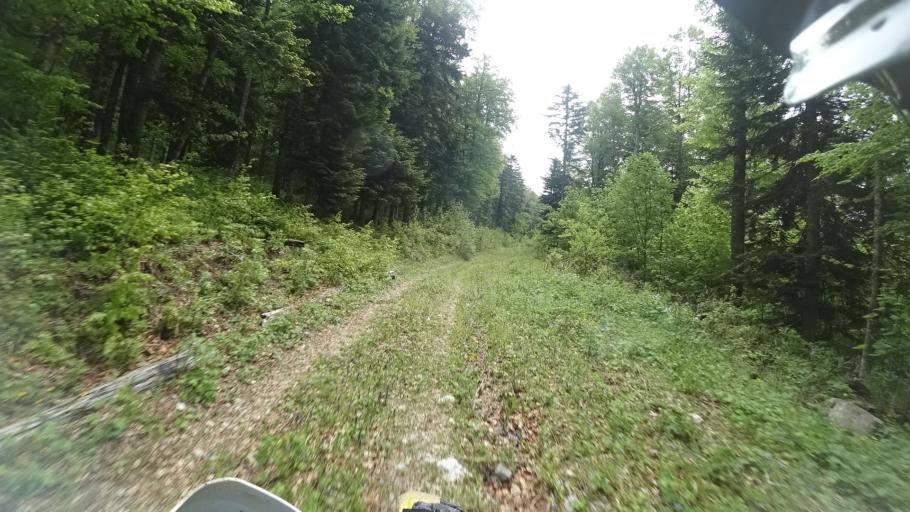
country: BA
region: Federation of Bosnia and Herzegovina
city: Orasac
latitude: 44.5708
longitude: 15.8673
